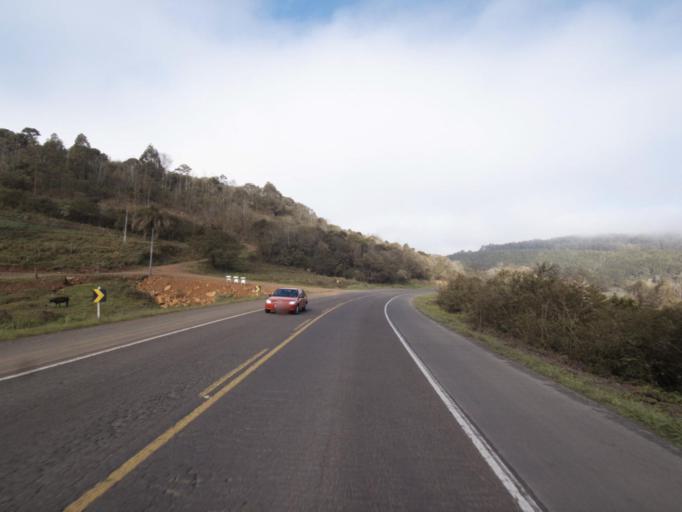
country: BR
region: Rio Grande do Sul
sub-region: Frederico Westphalen
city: Frederico Westphalen
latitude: -27.0156
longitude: -53.2274
